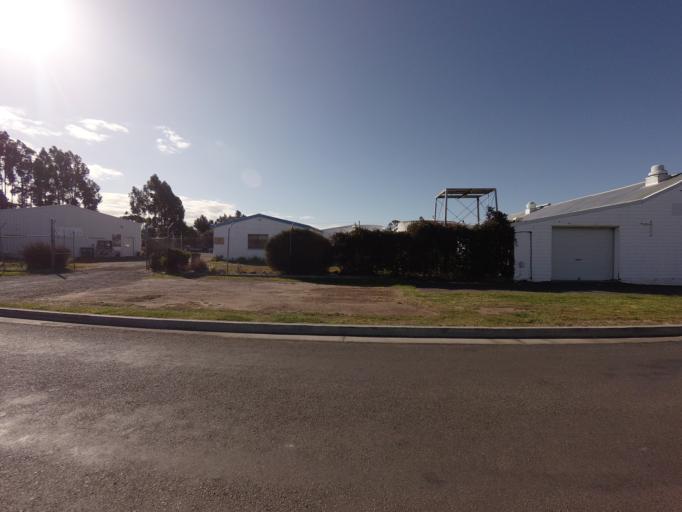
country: AU
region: Tasmania
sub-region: Sorell
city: Sorell
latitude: -42.5107
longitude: 147.9135
